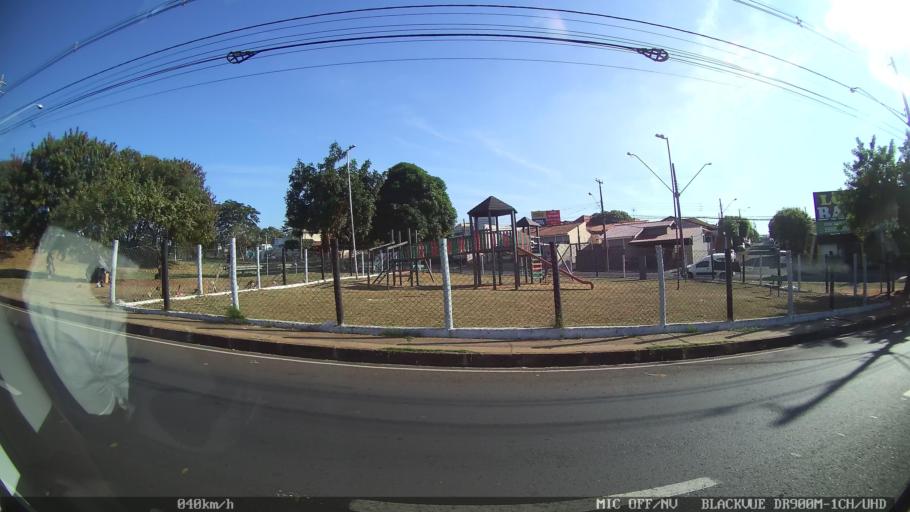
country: BR
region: Sao Paulo
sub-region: Sao Jose Do Rio Preto
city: Sao Jose do Rio Preto
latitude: -20.7675
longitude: -49.3857
